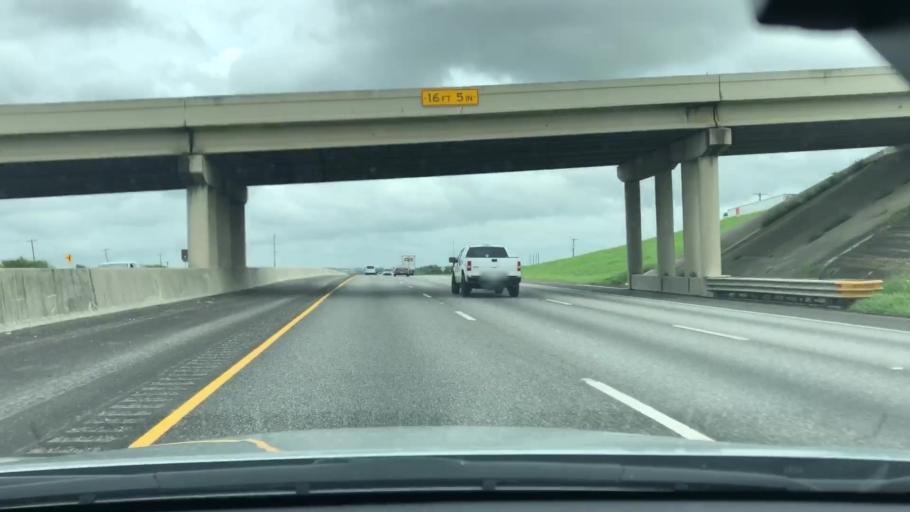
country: US
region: Texas
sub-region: Guadalupe County
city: Lake Dunlap
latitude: 29.7781
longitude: -98.0367
